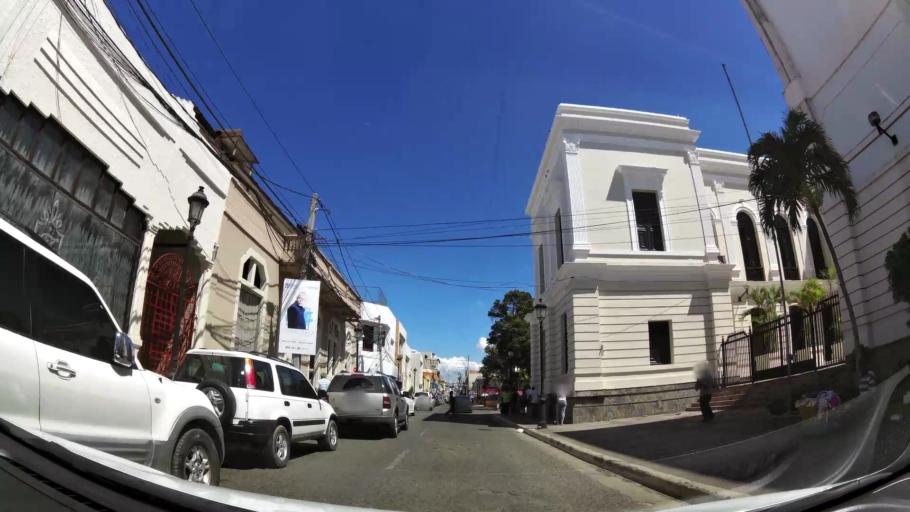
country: DO
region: Santiago
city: Santiago de los Caballeros
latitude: 19.4513
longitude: -70.7071
